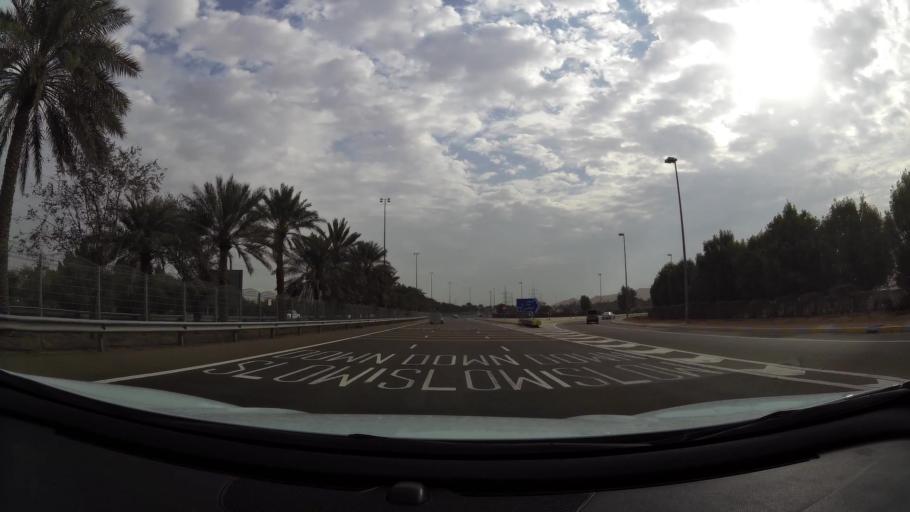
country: AE
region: Abu Dhabi
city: Al Ain
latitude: 24.2236
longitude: 55.5569
